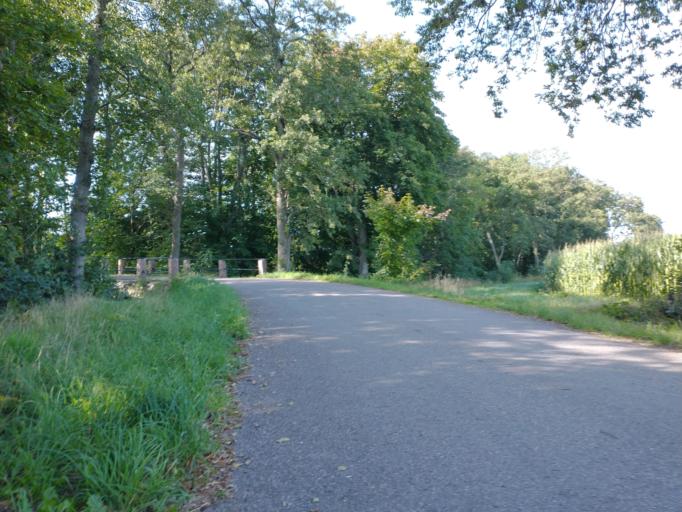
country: SE
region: Kalmar
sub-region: Kalmar Kommun
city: Lindsdal
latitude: 56.7845
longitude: 16.3213
